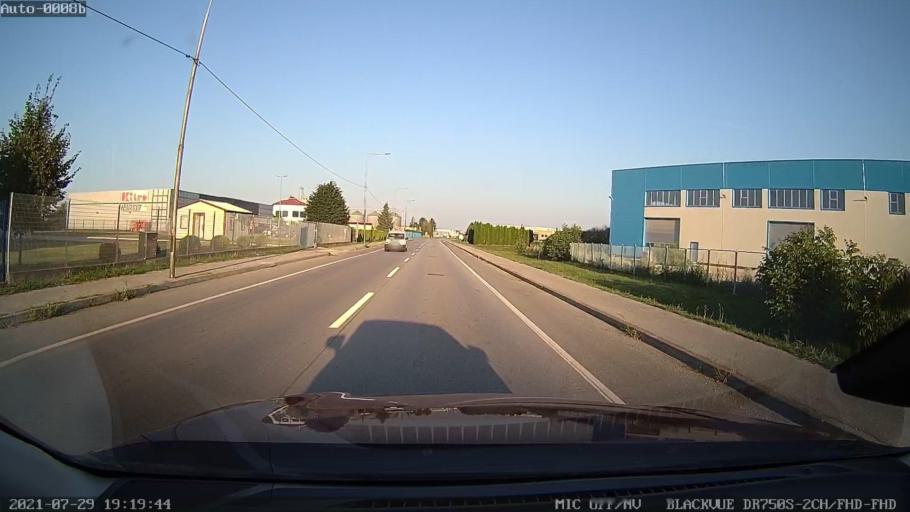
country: HR
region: Varazdinska
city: Ludbreg
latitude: 46.2569
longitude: 16.6012
